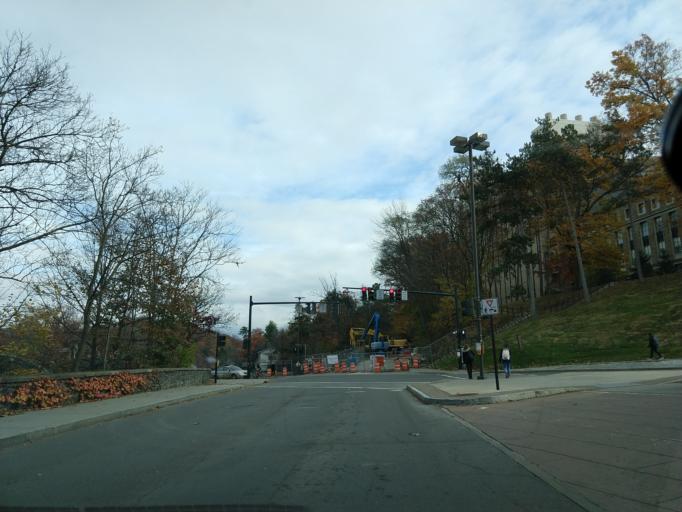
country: US
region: New York
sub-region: Tompkins County
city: Cayuga Heights
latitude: 42.4514
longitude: -76.4826
